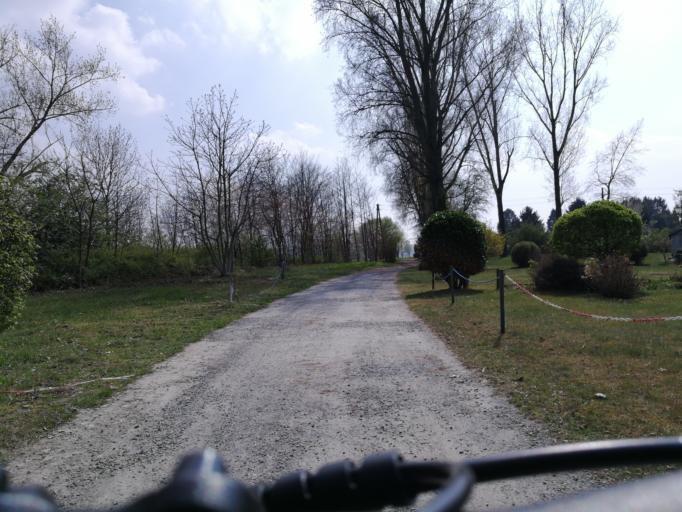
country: DE
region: North Rhine-Westphalia
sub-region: Regierungsbezirk Dusseldorf
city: Dormagen
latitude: 51.1572
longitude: 6.8540
